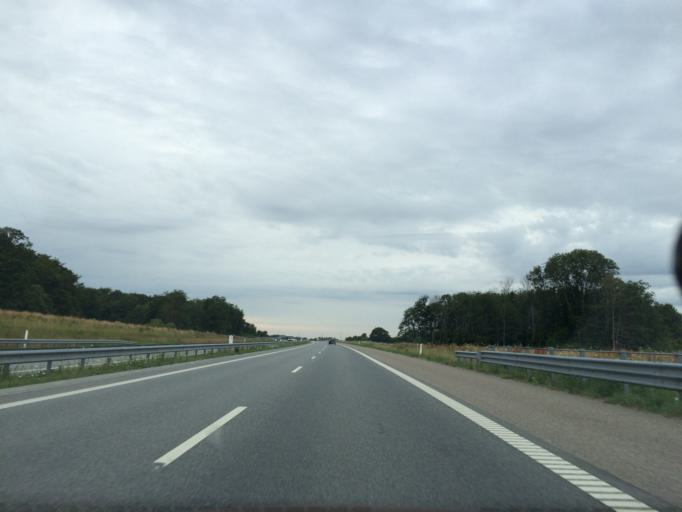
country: DK
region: South Denmark
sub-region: Sonderborg Kommune
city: Grasten
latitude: 54.9519
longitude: 9.6377
